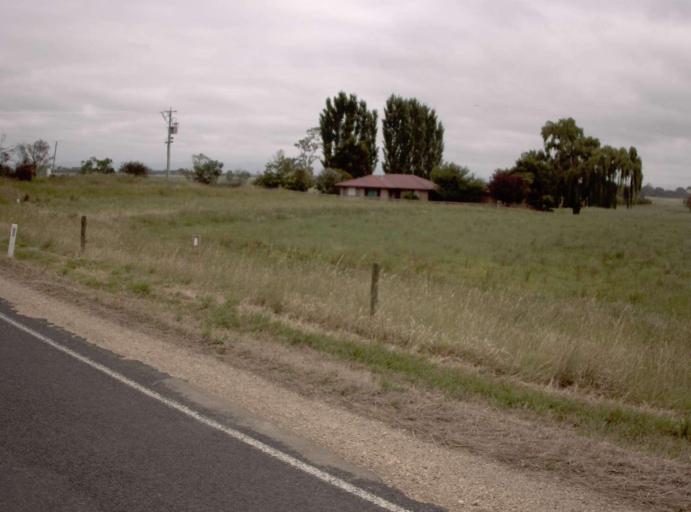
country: AU
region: Victoria
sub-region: Wellington
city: Heyfield
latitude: -38.0314
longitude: 146.9174
